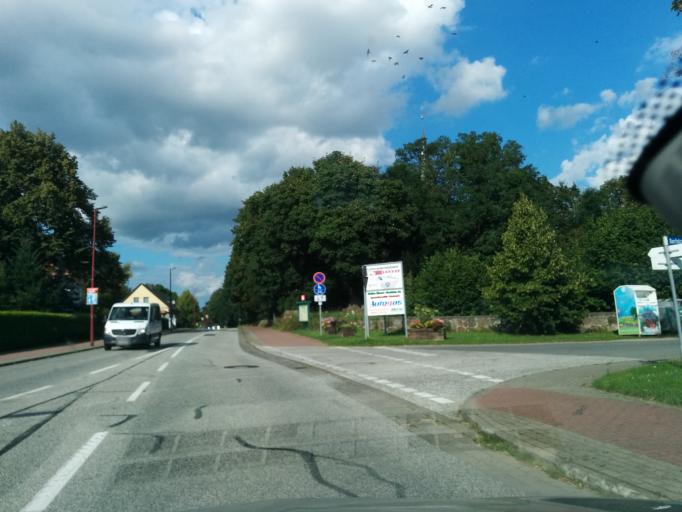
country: DE
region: Mecklenburg-Vorpommern
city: Pasewalk
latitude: 53.4729
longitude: 13.9782
